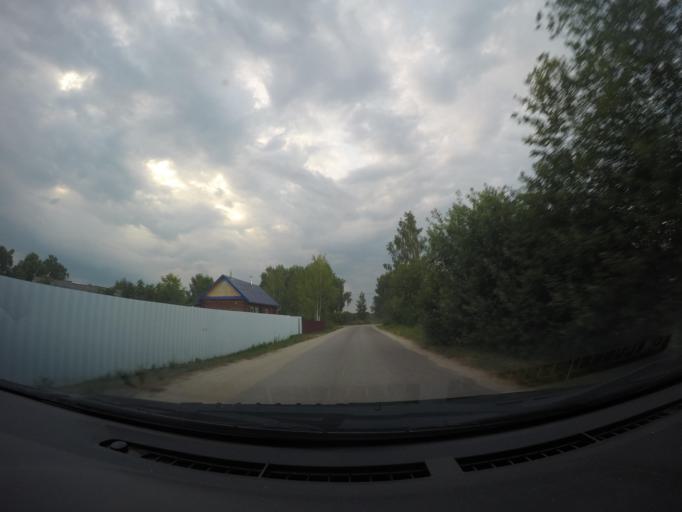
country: RU
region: Moskovskaya
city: Krasnyy Tkach
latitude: 55.3842
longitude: 39.2036
